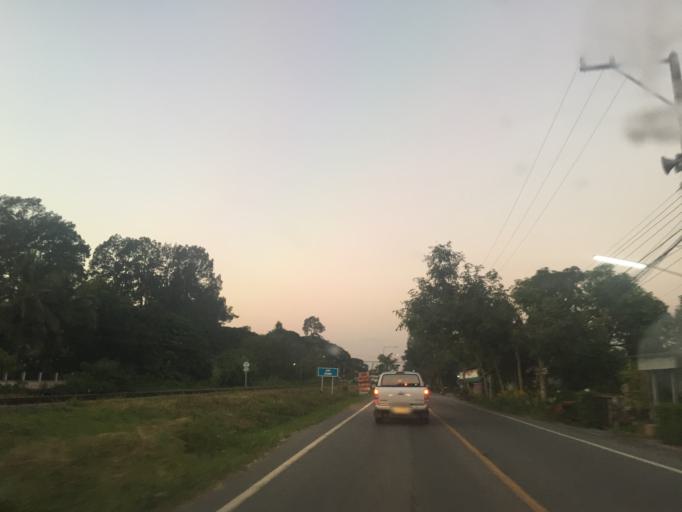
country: TH
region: Chiang Mai
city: Saraphi
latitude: 18.6918
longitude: 99.0454
